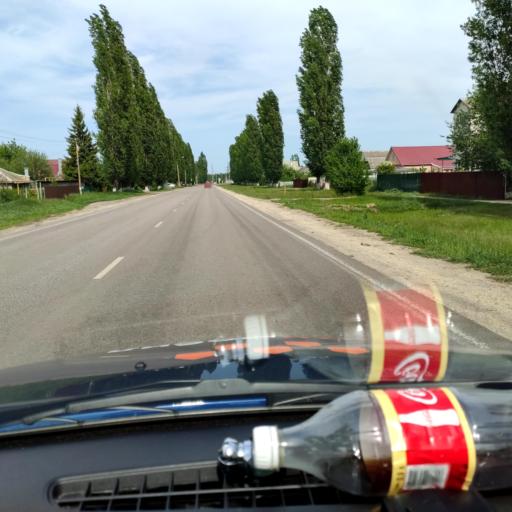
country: RU
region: Voronezj
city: Novaya Usman'
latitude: 51.5428
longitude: 39.3503
